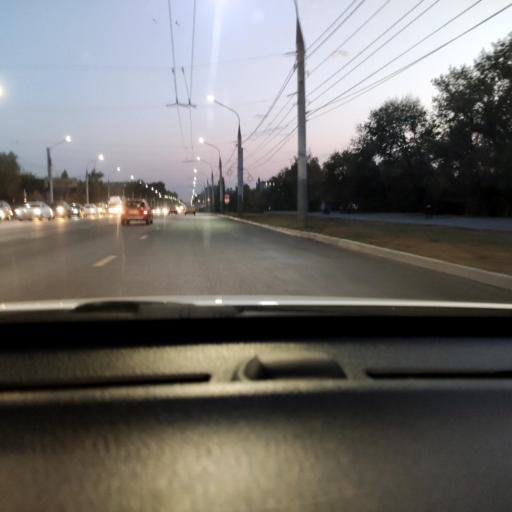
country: RU
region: Voronezj
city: Voronezh
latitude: 51.6618
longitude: 39.2470
